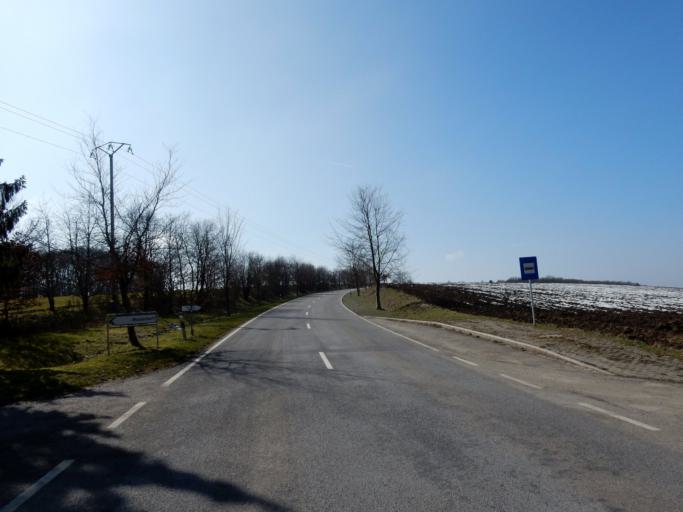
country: LU
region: Diekirch
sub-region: Canton de Wiltz
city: Bavigne
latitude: 49.8928
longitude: 5.8721
